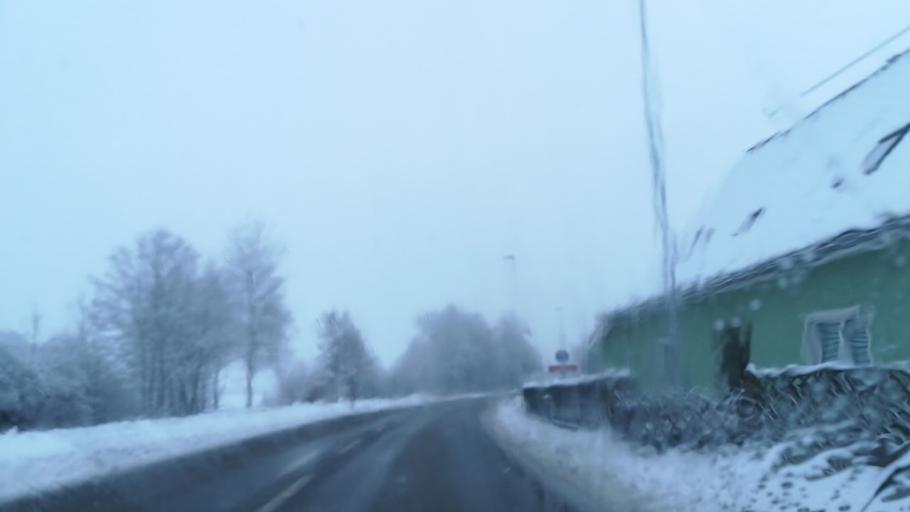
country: AT
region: Styria
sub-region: Politischer Bezirk Murtal
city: Knittelfeld
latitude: 47.2223
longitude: 14.8013
